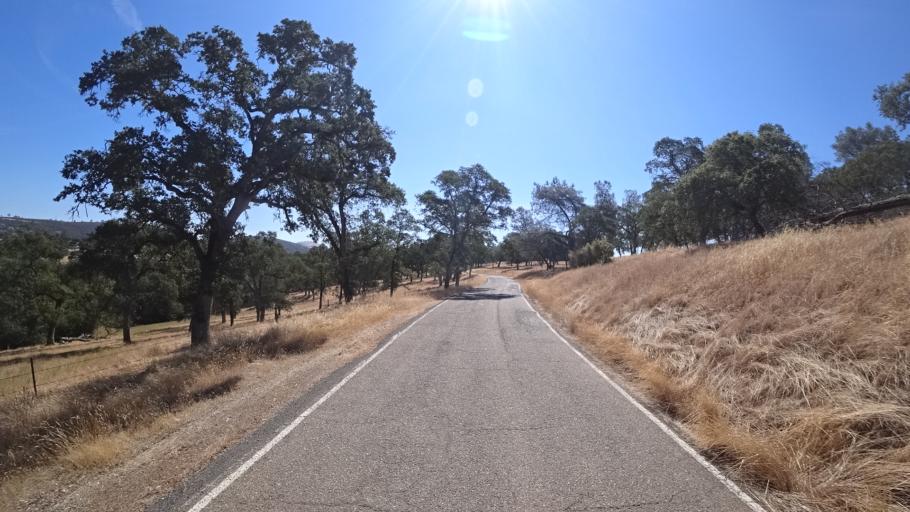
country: US
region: California
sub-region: Calaveras County
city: Valley Springs
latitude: 38.2261
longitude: -120.8266
